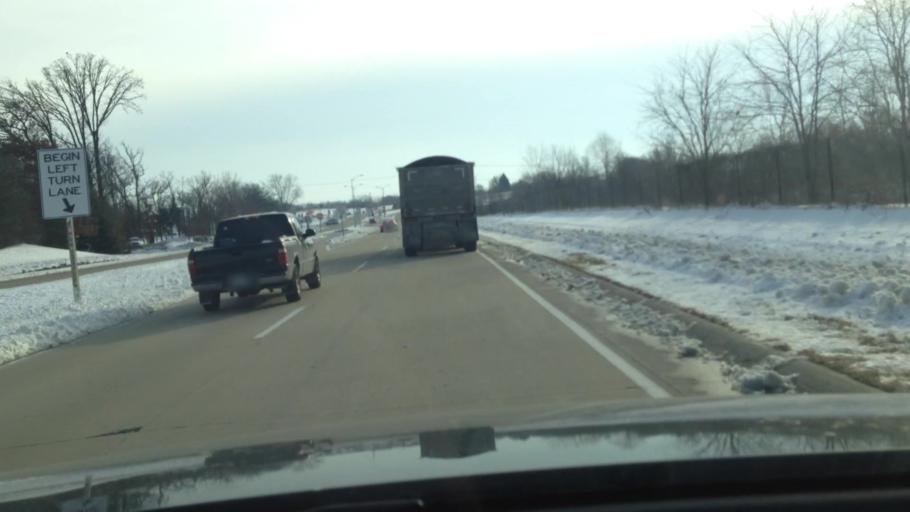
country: US
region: Wisconsin
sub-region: Walworth County
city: Lake Geneva
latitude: 42.5672
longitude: -88.4136
